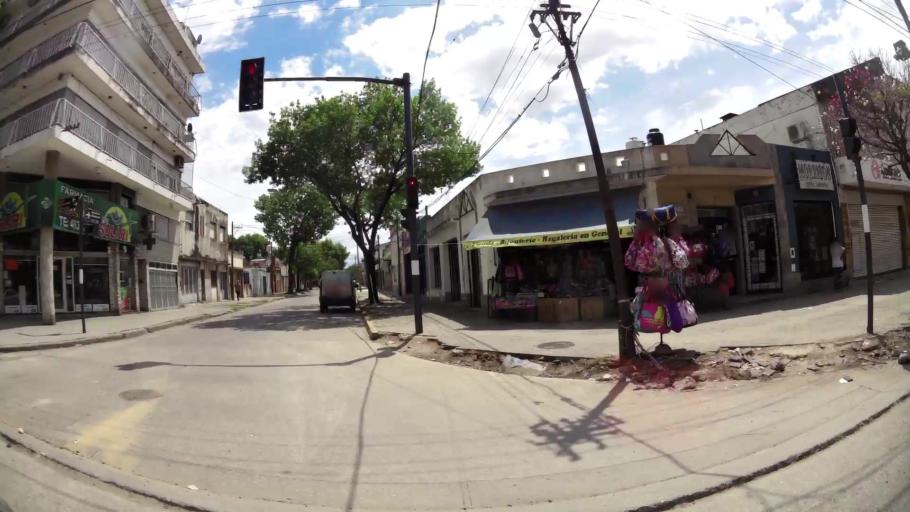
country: AR
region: Santa Fe
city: Gobernador Galvez
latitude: -33.0020
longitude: -60.6493
